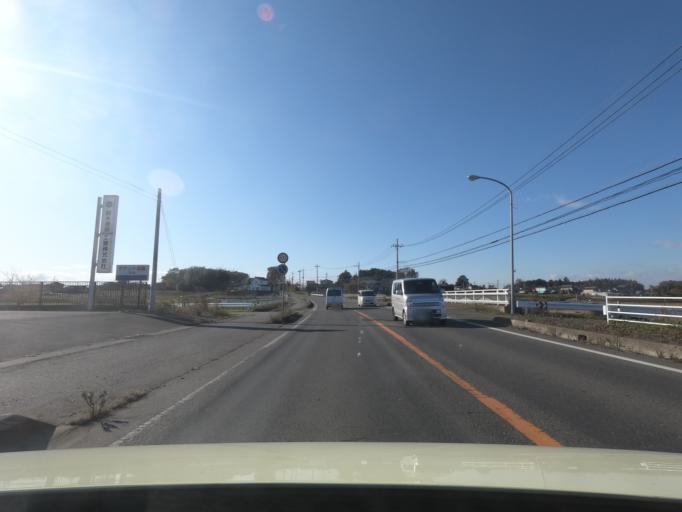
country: JP
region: Ibaraki
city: Koga
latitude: 36.2016
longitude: 139.8043
